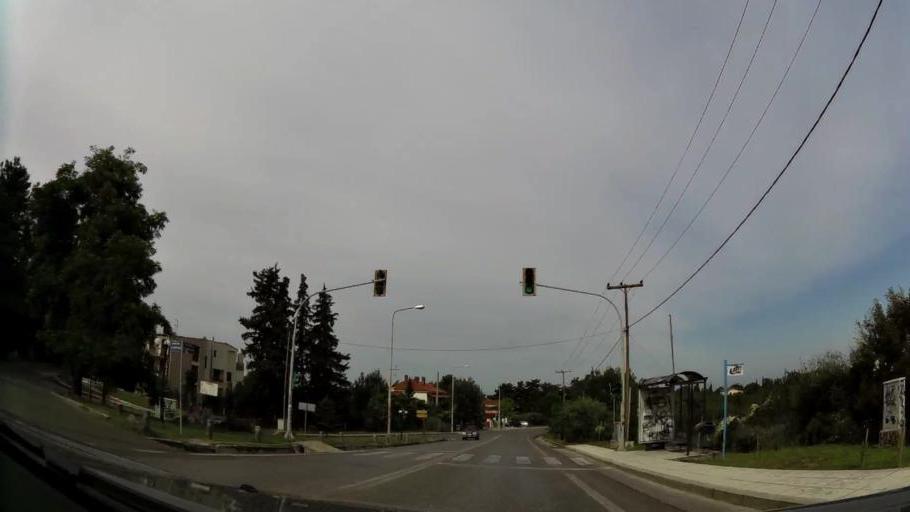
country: GR
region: Central Macedonia
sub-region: Nomos Thessalonikis
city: Panorama
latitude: 40.5918
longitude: 23.0280
